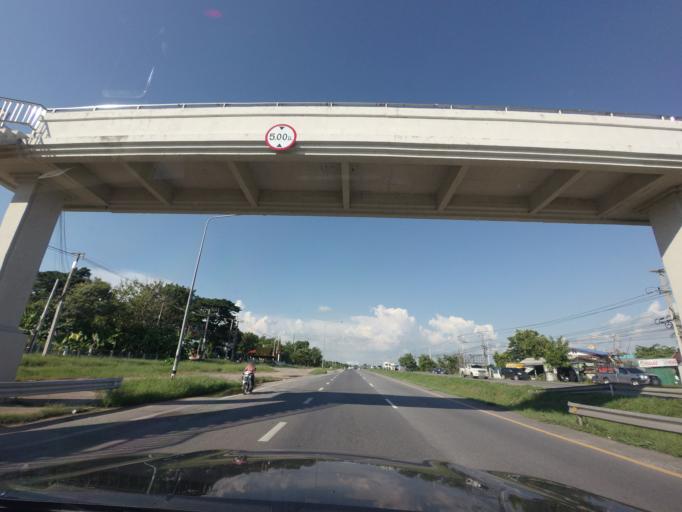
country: TH
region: Khon Kaen
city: Non Sila
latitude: 15.9515
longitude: 102.6836
